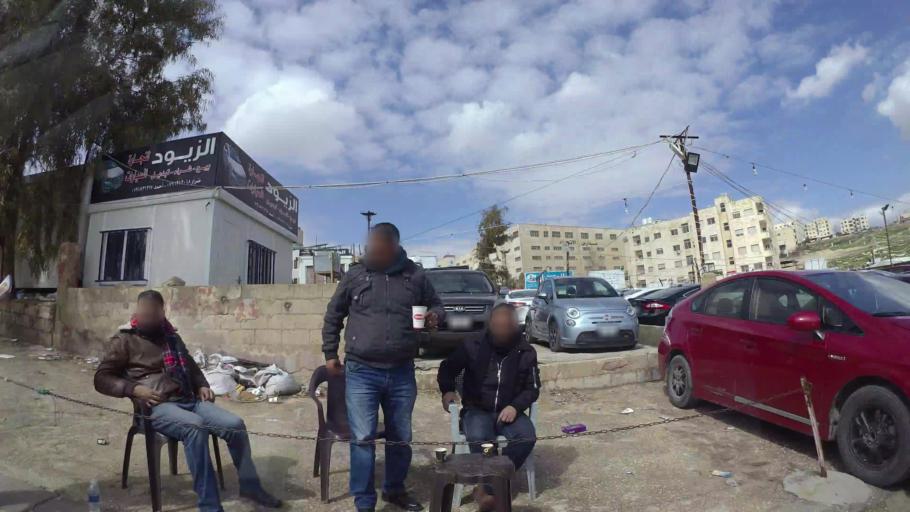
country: JO
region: Amman
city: Amman
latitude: 31.9949
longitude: 35.9166
